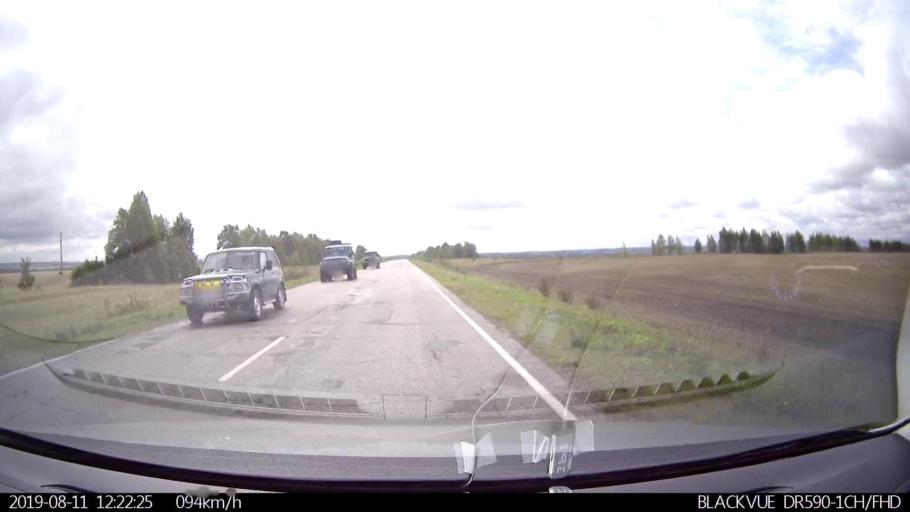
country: RU
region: Ulyanovsk
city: Ignatovka
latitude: 53.9080
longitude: 47.9544
